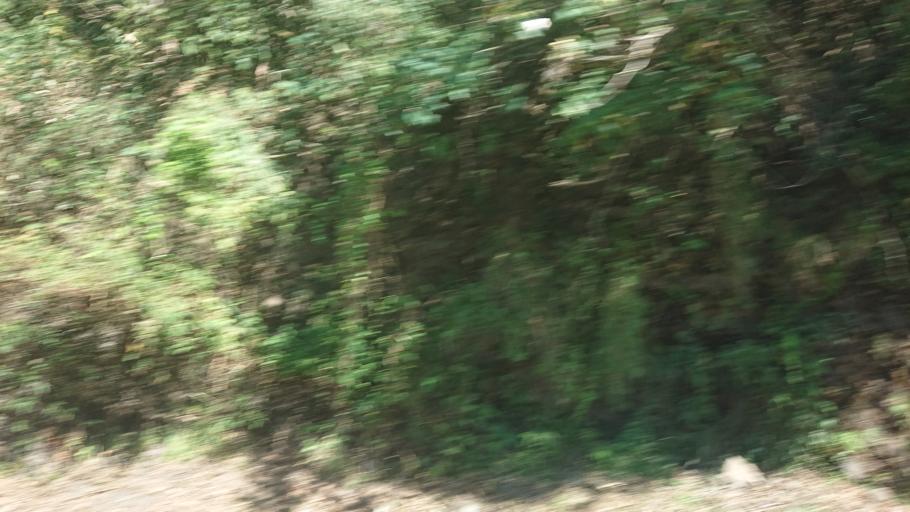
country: TW
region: Taiwan
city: Lugu
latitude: 23.4912
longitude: 120.7735
